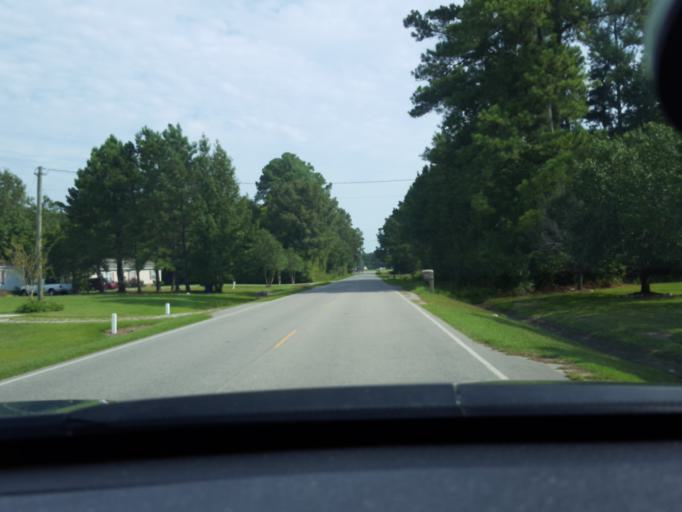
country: US
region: North Carolina
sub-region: Washington County
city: Plymouth
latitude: 35.8879
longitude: -76.7058
